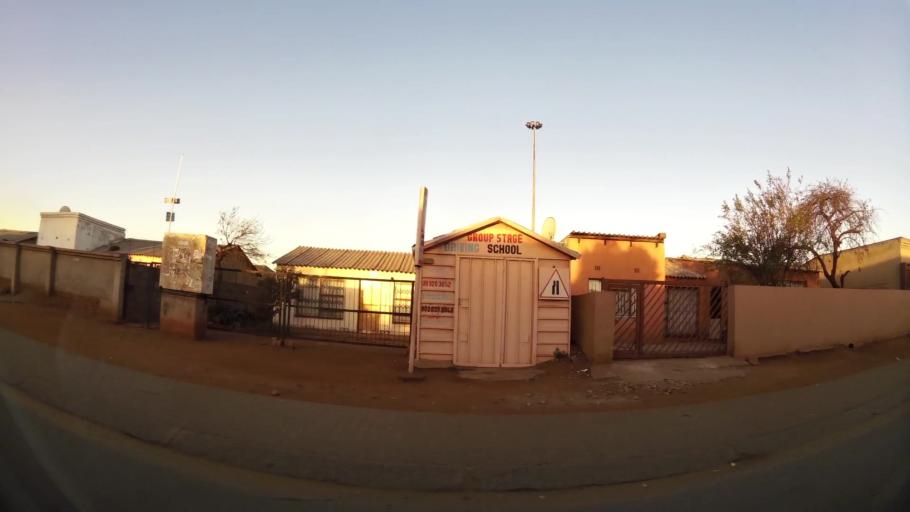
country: ZA
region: Gauteng
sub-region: Ekurhuleni Metropolitan Municipality
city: Tembisa
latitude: -25.9963
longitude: 28.2270
